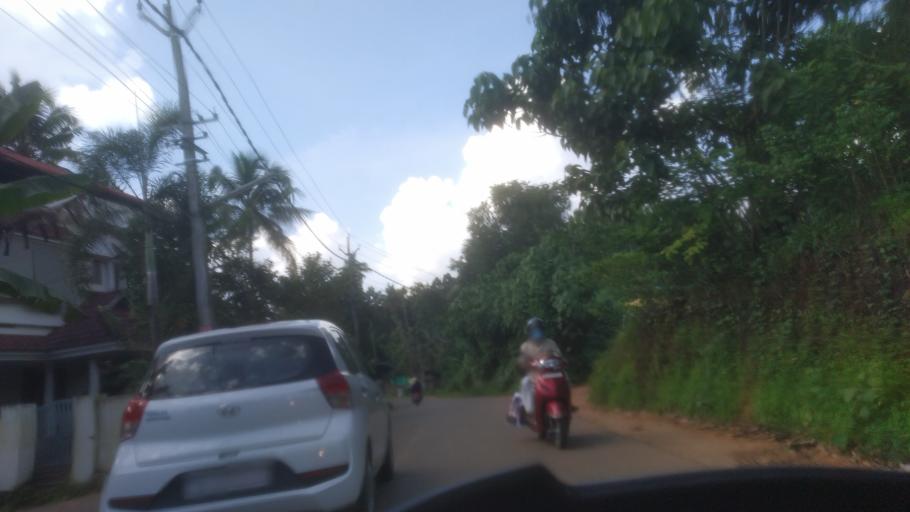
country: IN
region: Kerala
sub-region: Ernakulam
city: Muvattupula
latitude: 9.9958
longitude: 76.6033
